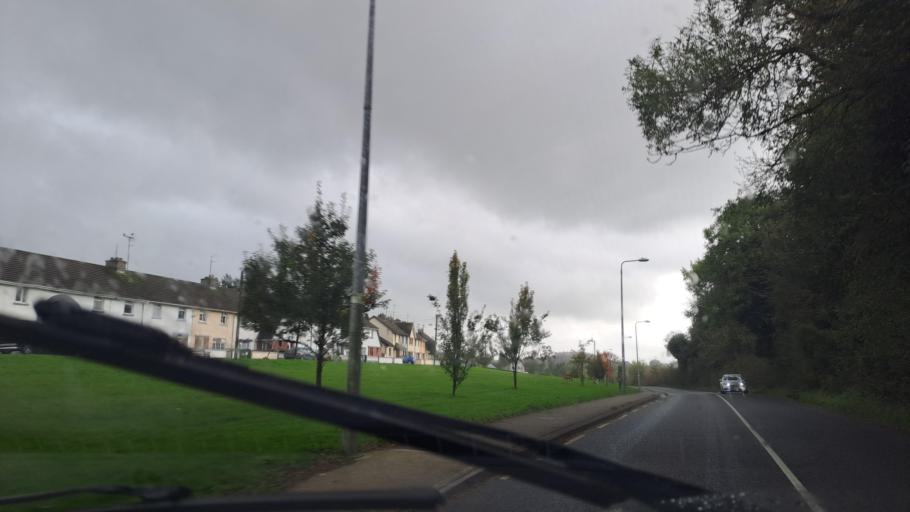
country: IE
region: Ulster
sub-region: An Cabhan
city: Bailieborough
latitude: 53.9214
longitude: -6.9804
